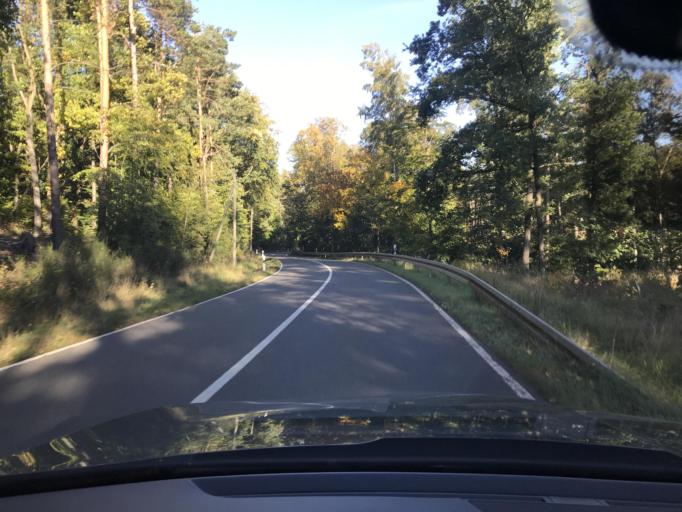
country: DE
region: Saxony-Anhalt
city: Thale
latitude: 51.7245
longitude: 11.0264
